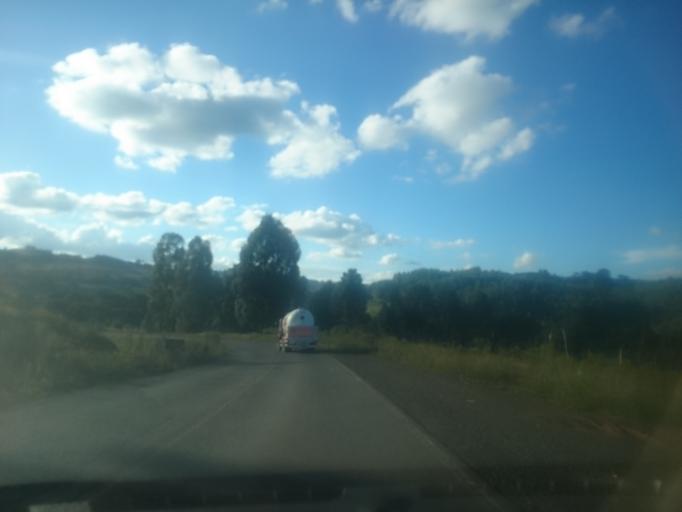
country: BR
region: Santa Catarina
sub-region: Sao Joaquim
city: Sao Joaquim
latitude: -28.0924
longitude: -50.0566
